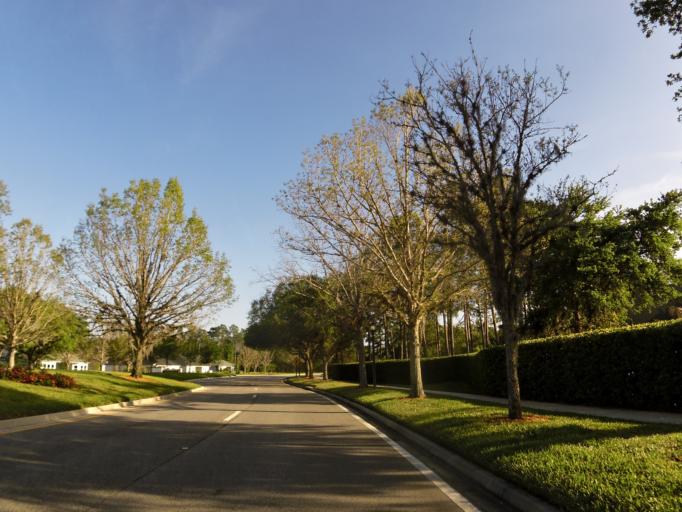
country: US
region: Florida
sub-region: Saint Johns County
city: Villano Beach
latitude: 29.9795
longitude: -81.4768
